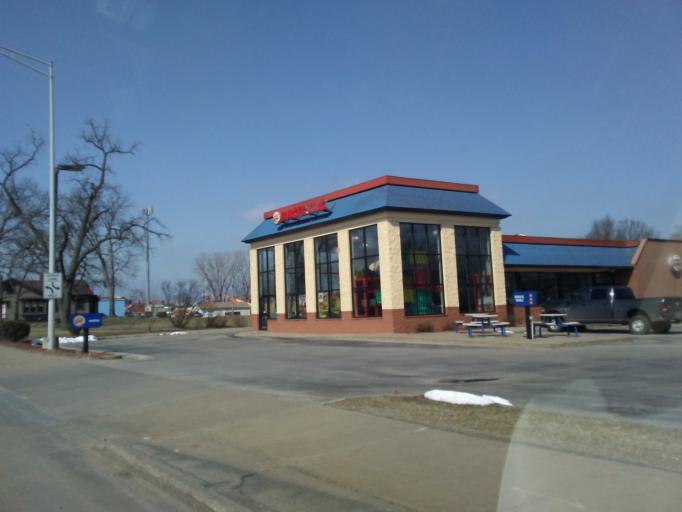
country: US
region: Wisconsin
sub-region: La Crosse County
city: La Crosse
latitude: 43.7801
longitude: -91.2251
